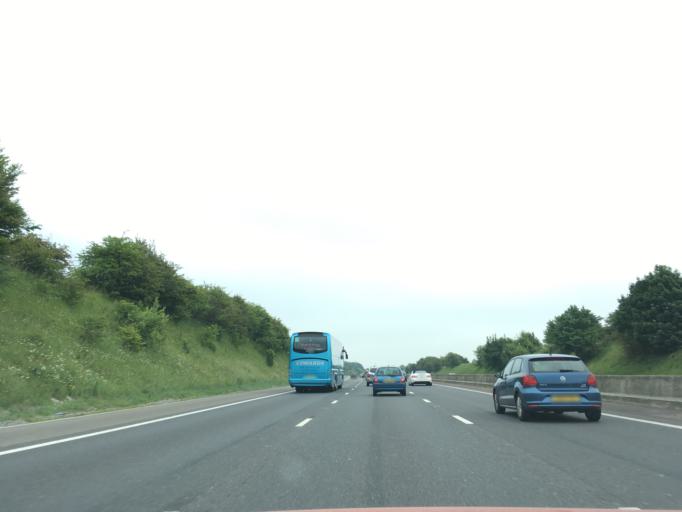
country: GB
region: England
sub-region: Wiltshire
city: Aldbourne
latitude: 51.5079
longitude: -1.6081
